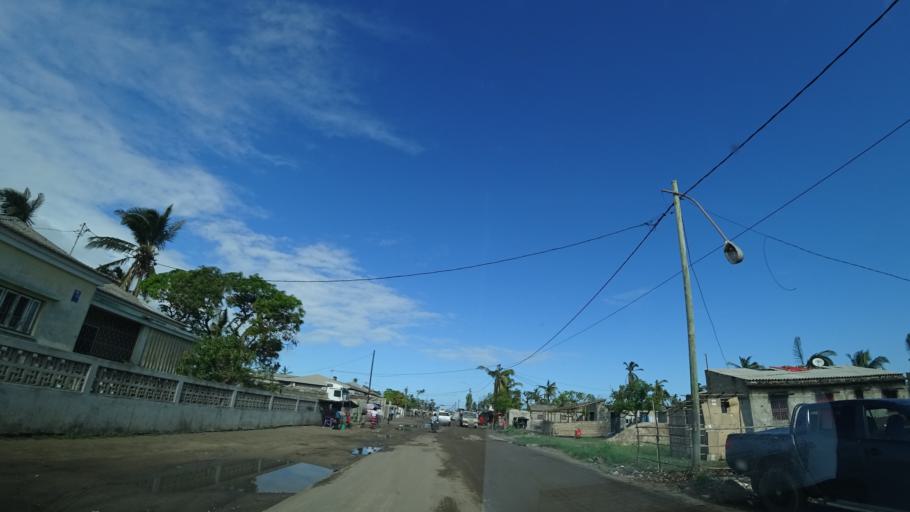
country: MZ
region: Sofala
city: Beira
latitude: -19.7877
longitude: 34.8837
